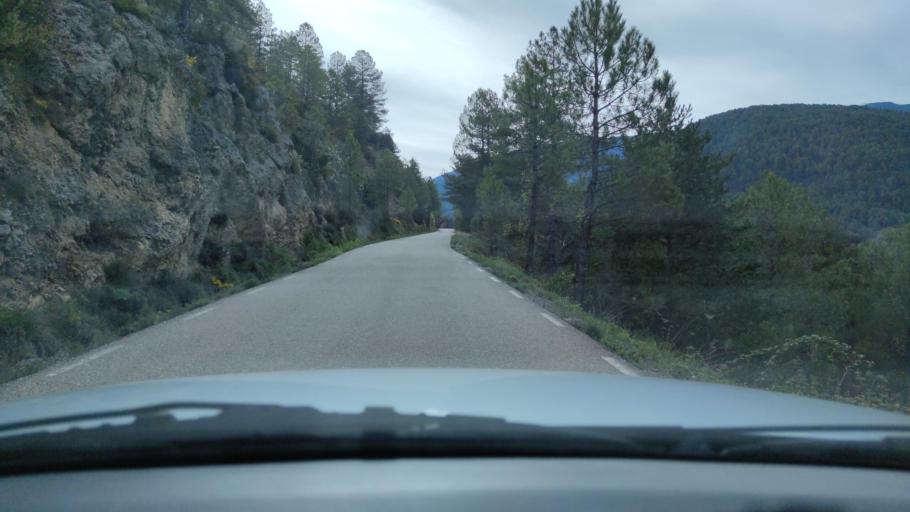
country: ES
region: Catalonia
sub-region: Provincia de Lleida
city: Alas i Cerc
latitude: 42.2342
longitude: 1.4707
